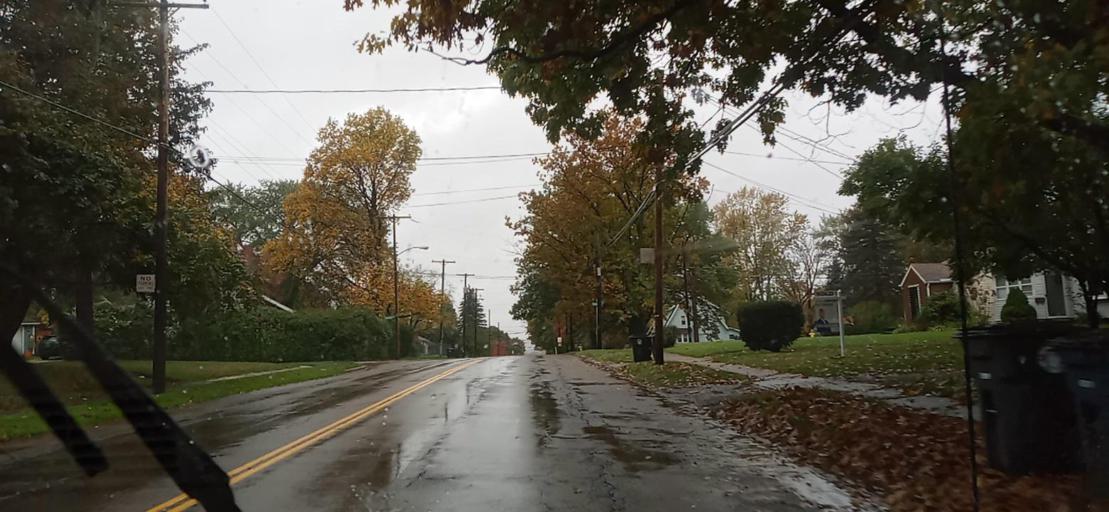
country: US
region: Ohio
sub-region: Summit County
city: Akron
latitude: 41.0557
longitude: -81.5619
